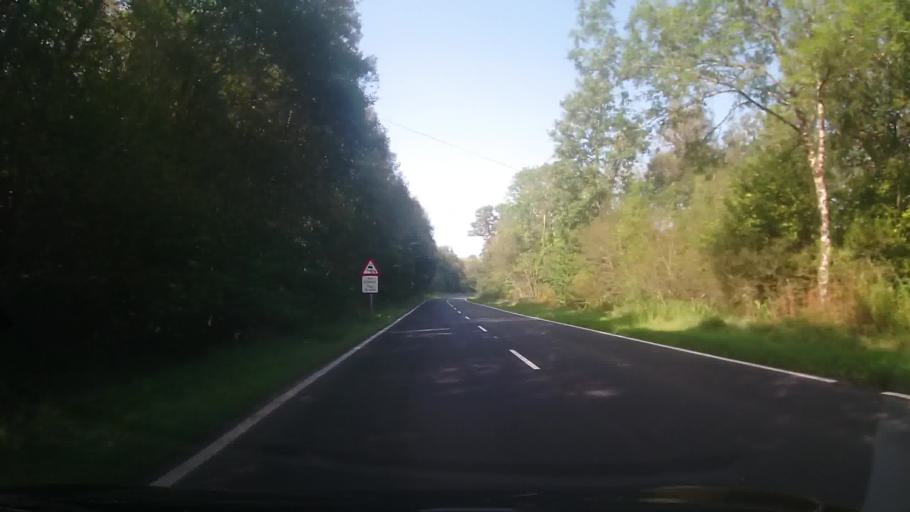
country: GB
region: Wales
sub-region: Sir Powys
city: Builth Wells
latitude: 52.1339
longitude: -3.5436
